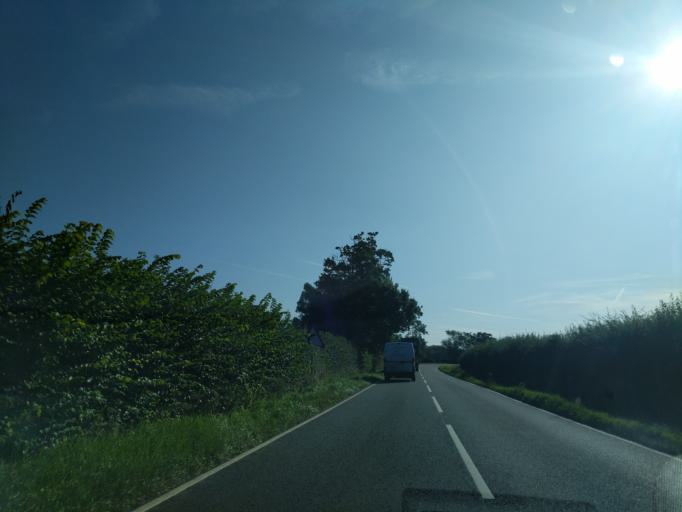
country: GB
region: England
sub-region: Lincolnshire
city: Bourne
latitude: 52.8019
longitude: -0.4586
